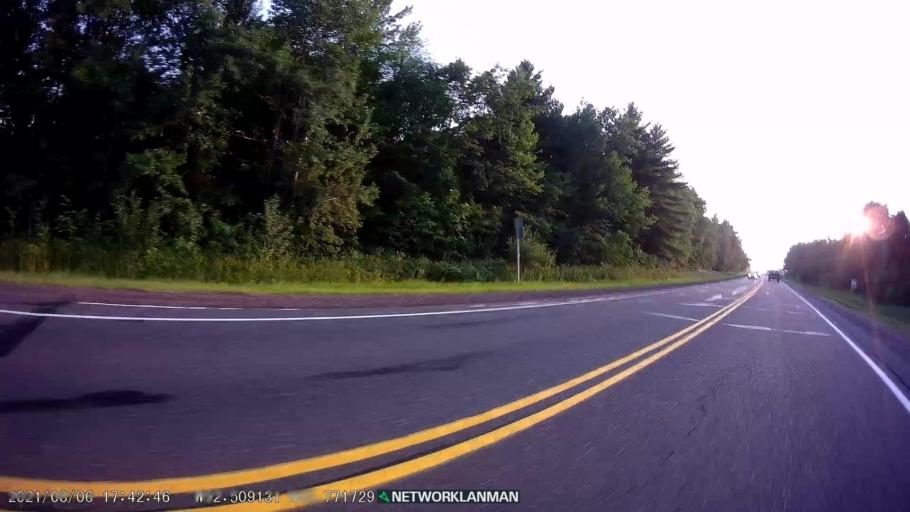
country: US
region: Wisconsin
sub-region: Polk County
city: Frederic
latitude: 45.7717
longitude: -92.5099
